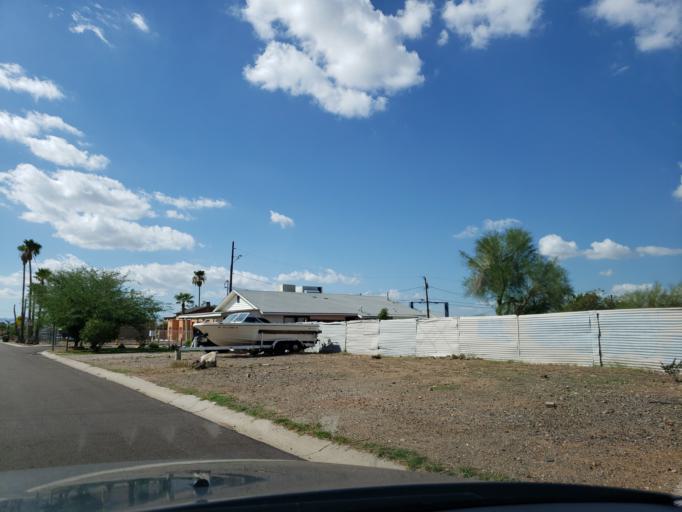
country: US
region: Arizona
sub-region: Maricopa County
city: Glendale
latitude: 33.5799
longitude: -112.0848
